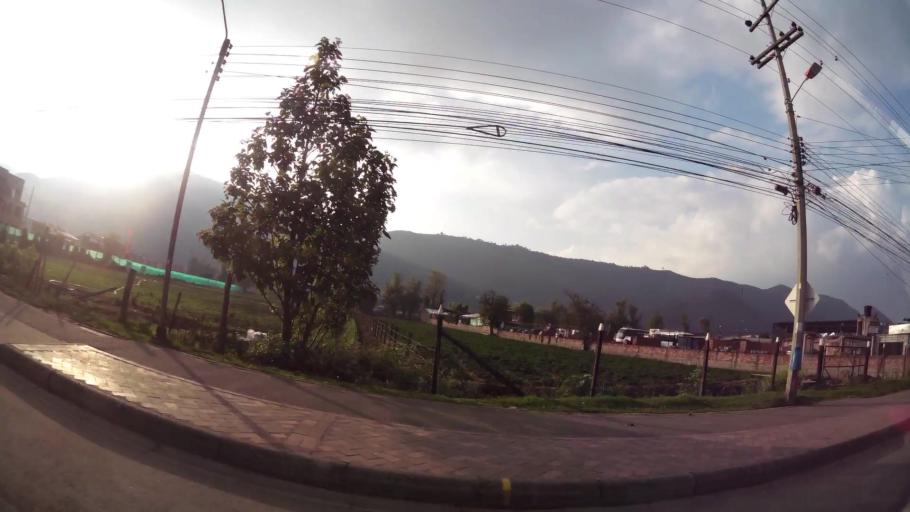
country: CO
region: Cundinamarca
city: Cota
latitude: 4.8148
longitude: -74.0979
